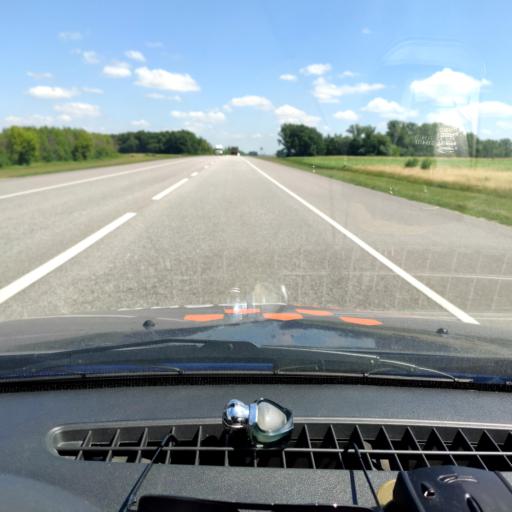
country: RU
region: Orjol
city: Orel
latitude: 52.8514
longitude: 36.2377
